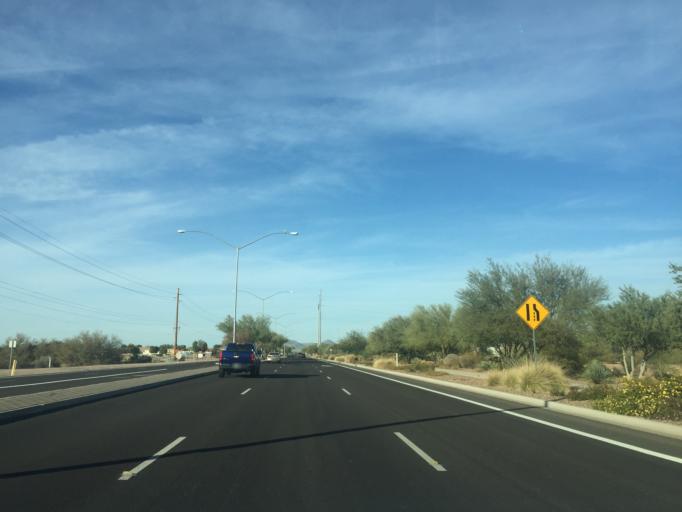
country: US
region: Arizona
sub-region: Maricopa County
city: Queen Creek
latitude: 33.3540
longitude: -111.6357
